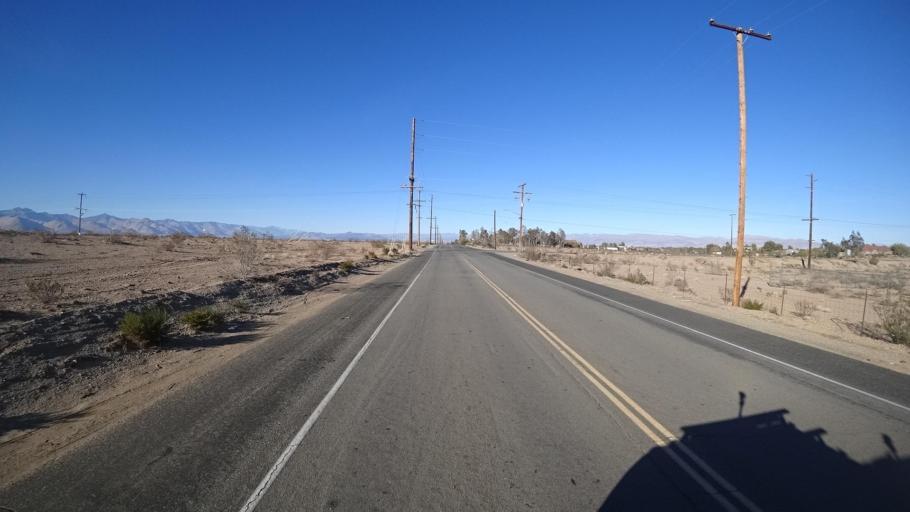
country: US
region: California
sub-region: Kern County
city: China Lake Acres
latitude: 35.6220
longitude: -117.7230
